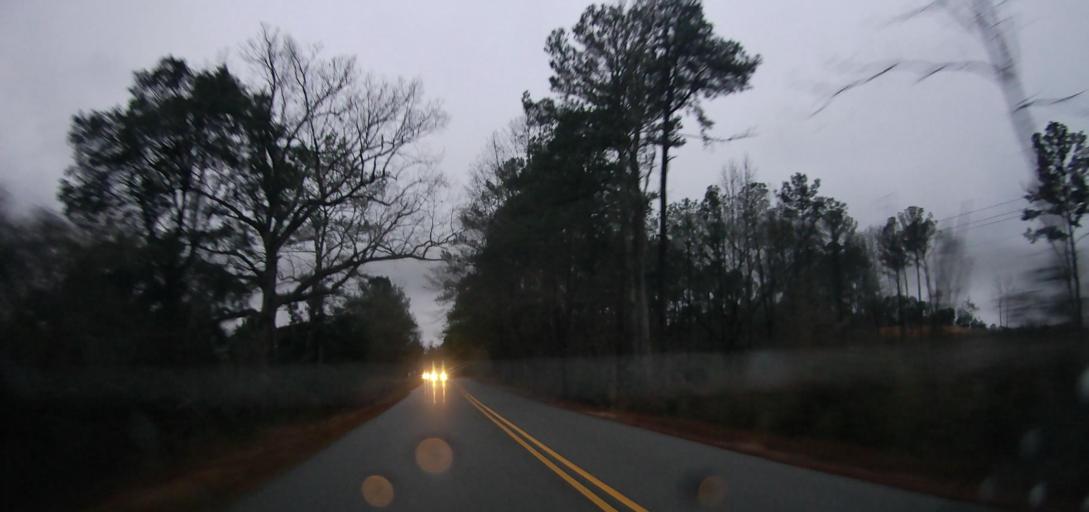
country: US
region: Alabama
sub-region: Tuscaloosa County
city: Vance
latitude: 33.1338
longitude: -87.2297
